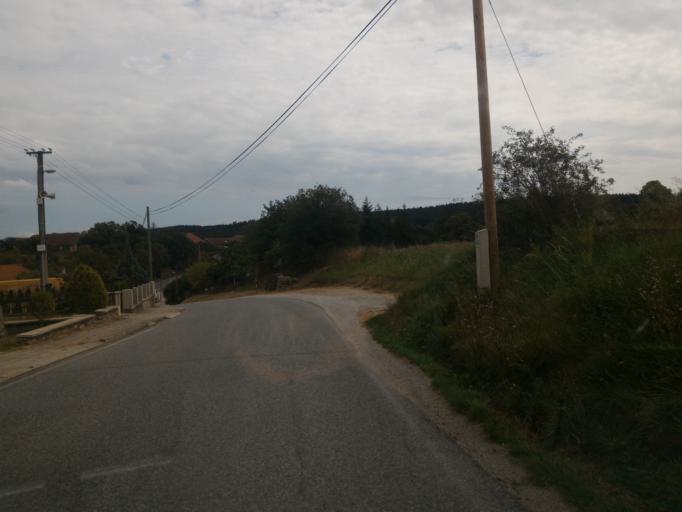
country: CZ
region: Vysocina
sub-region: Okres Jihlava
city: Telc
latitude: 49.1241
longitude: 15.5340
